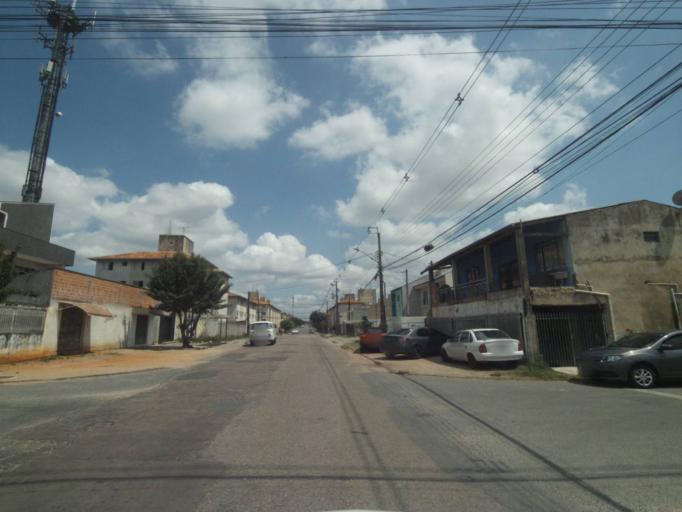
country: BR
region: Parana
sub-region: Sao Jose Dos Pinhais
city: Sao Jose dos Pinhais
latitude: -25.5448
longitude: -49.2539
